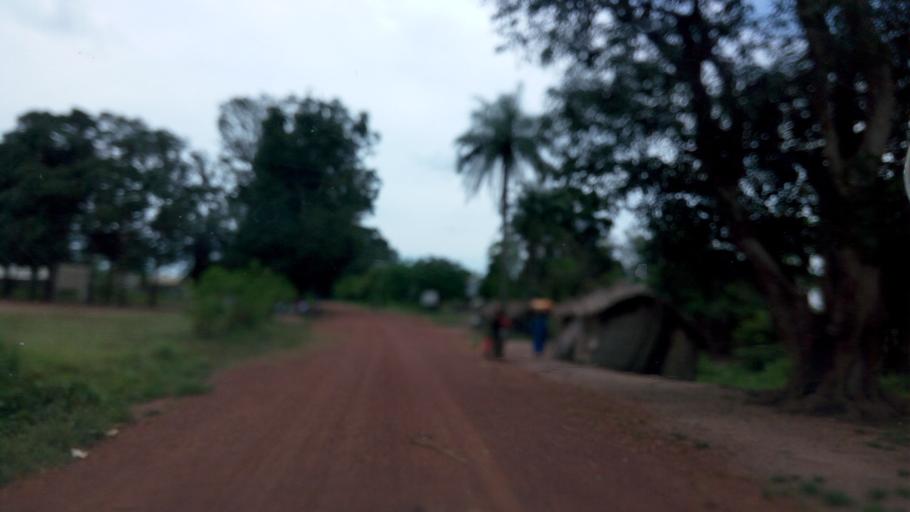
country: CD
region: Equateur
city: Libenge
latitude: 3.7287
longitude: 18.7727
